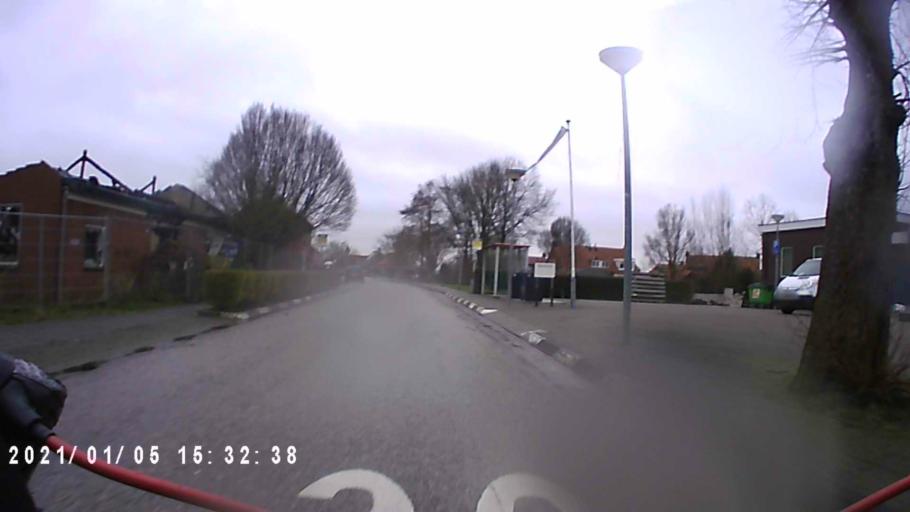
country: DE
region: Lower Saxony
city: Bunde
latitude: 53.2067
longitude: 7.1802
